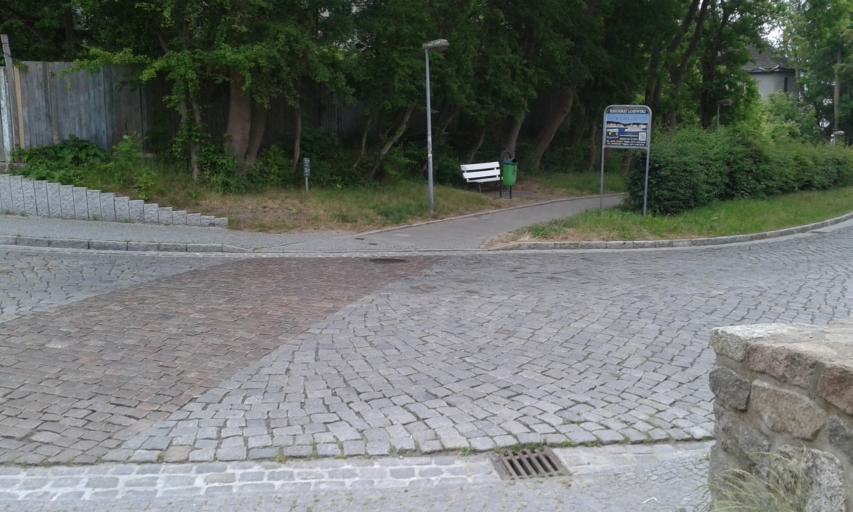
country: DE
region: Mecklenburg-Vorpommern
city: Sassnitz
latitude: 54.5162
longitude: 13.6492
